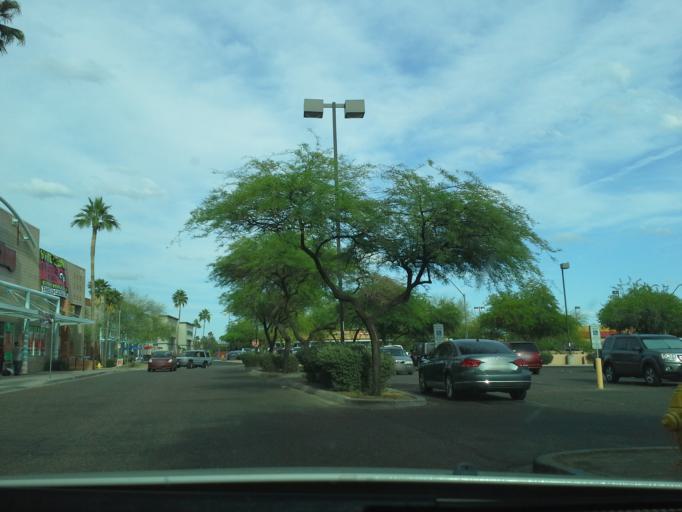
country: US
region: Arizona
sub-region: Maricopa County
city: Peoria
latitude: 33.6395
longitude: -112.2168
